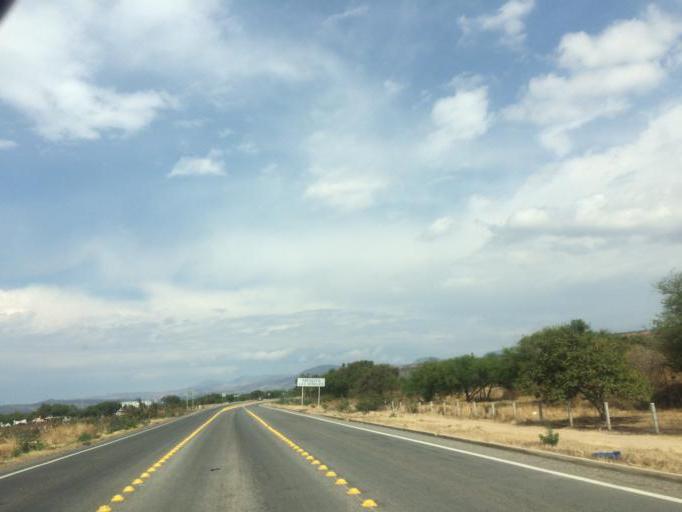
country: MX
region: Guanajuato
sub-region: Silao de la Victoria
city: Colonia Francisco Javier Mina
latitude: 21.0088
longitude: -101.4330
